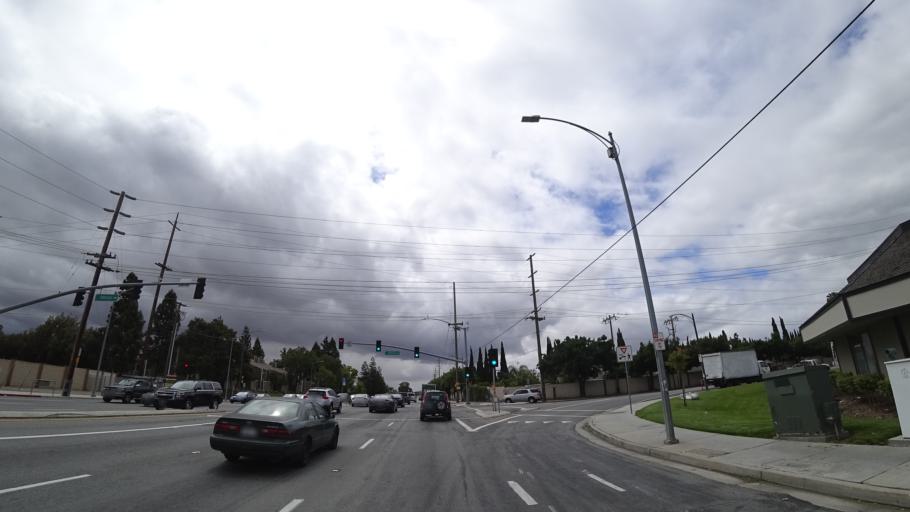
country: US
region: California
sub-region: Santa Clara County
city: Seven Trees
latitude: 37.3022
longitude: -121.8423
